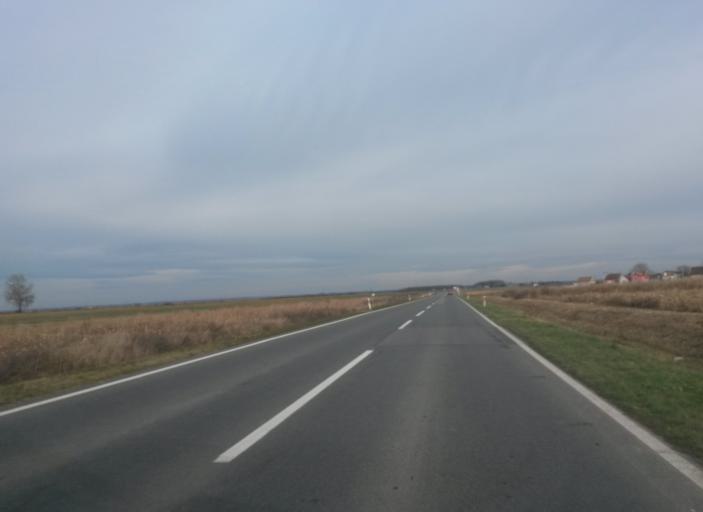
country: HR
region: Osjecko-Baranjska
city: Cepin
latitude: 45.5278
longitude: 18.5438
